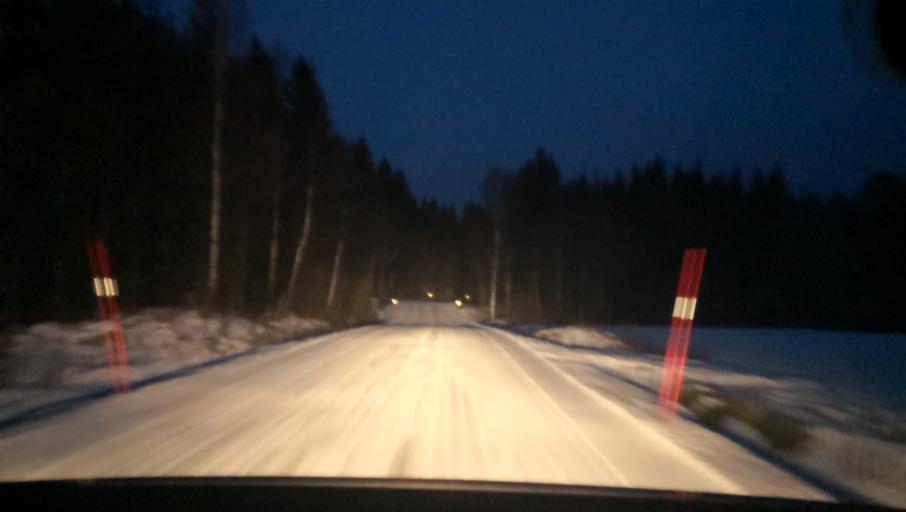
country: SE
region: Uppsala
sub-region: Heby Kommun
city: Tarnsjo
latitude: 60.2535
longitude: 16.7631
